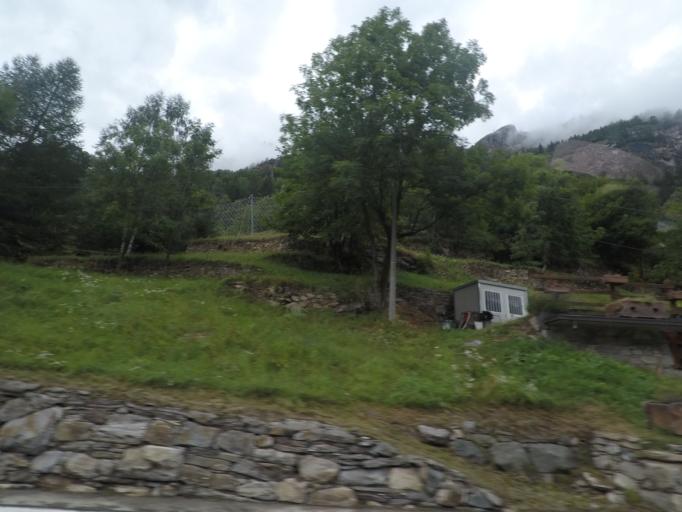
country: IT
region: Aosta Valley
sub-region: Valle d'Aosta
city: Valtournenche
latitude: 45.8644
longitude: 7.6111
